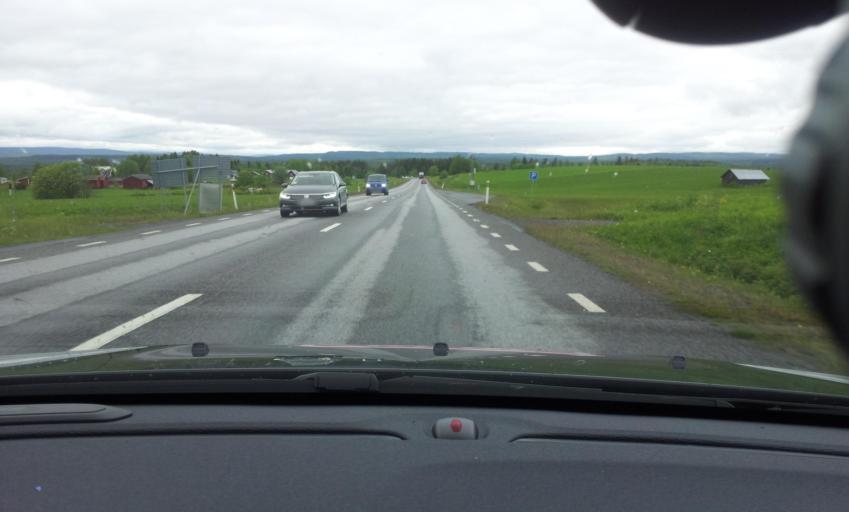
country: SE
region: Jaemtland
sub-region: Krokoms Kommun
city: Valla
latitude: 63.3050
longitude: 13.8796
